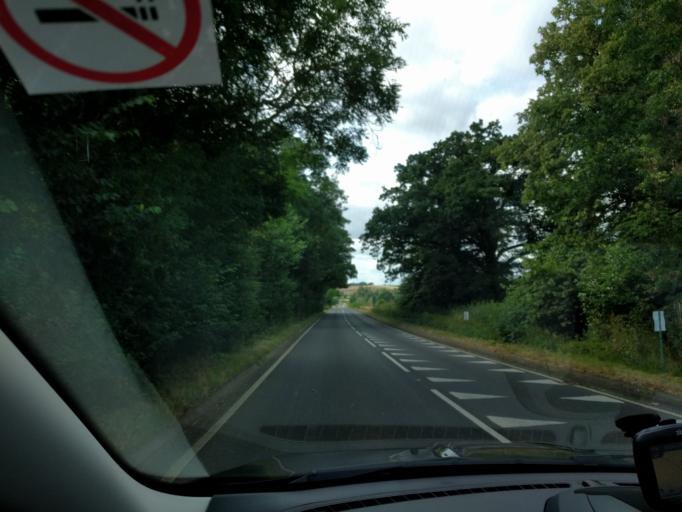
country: GB
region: England
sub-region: Warwickshire
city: Shipston on Stour
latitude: 52.1181
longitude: -1.6432
